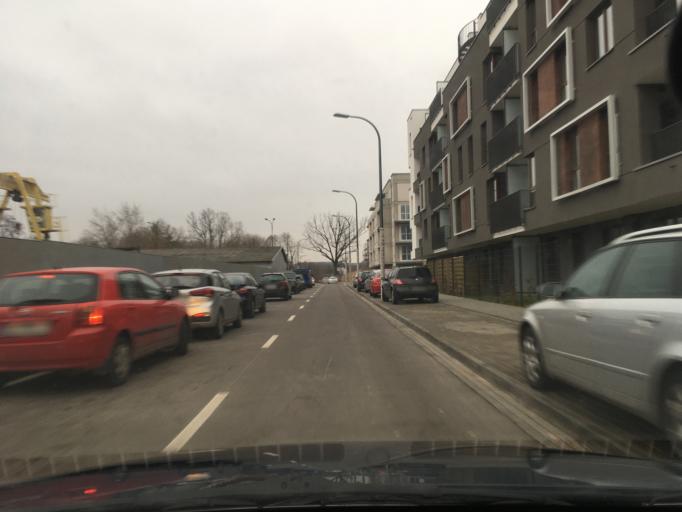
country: PL
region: Masovian Voivodeship
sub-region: Warszawa
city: Mokotow
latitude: 52.1613
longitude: 20.9963
